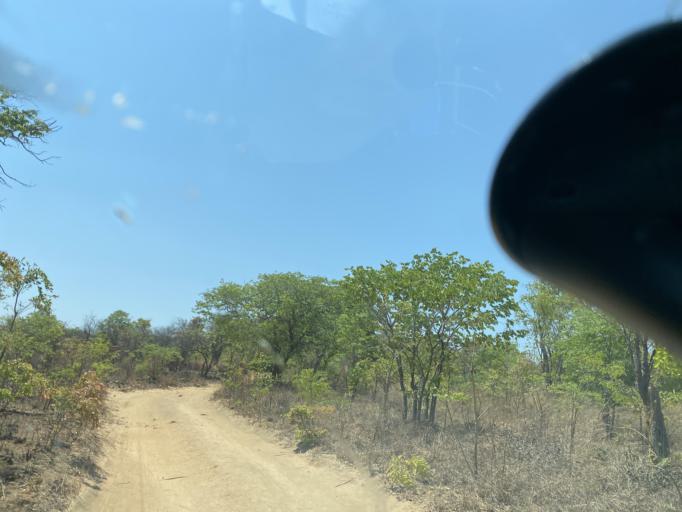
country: ZM
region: Lusaka
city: Chongwe
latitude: -15.4400
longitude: 29.2033
